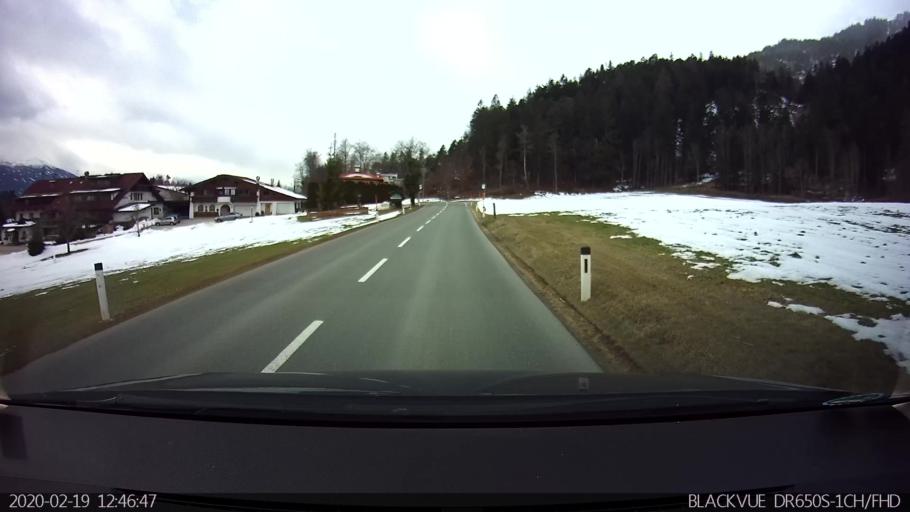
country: AT
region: Tyrol
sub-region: Politischer Bezirk Innsbruck Land
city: Gnadenwald
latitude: 47.3236
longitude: 11.5774
